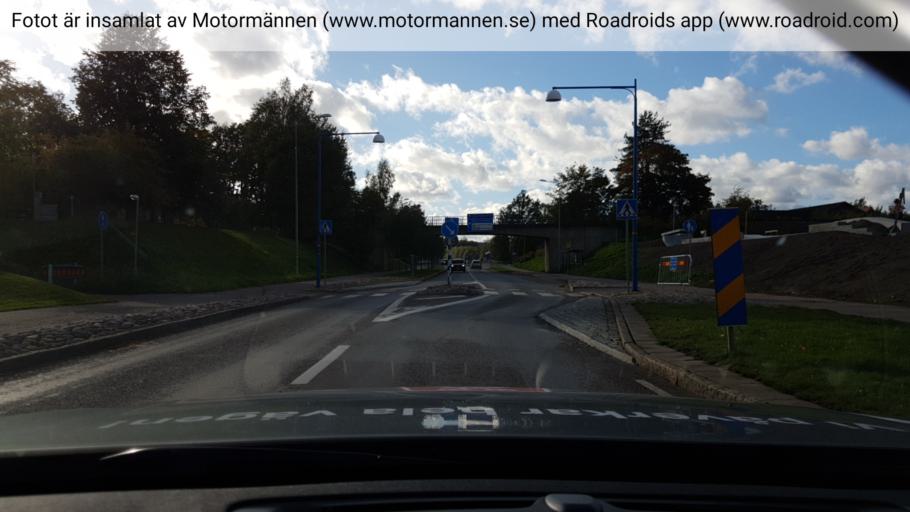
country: SE
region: Vaermland
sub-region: Filipstads Kommun
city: Filipstad
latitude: 59.7137
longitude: 14.1621
